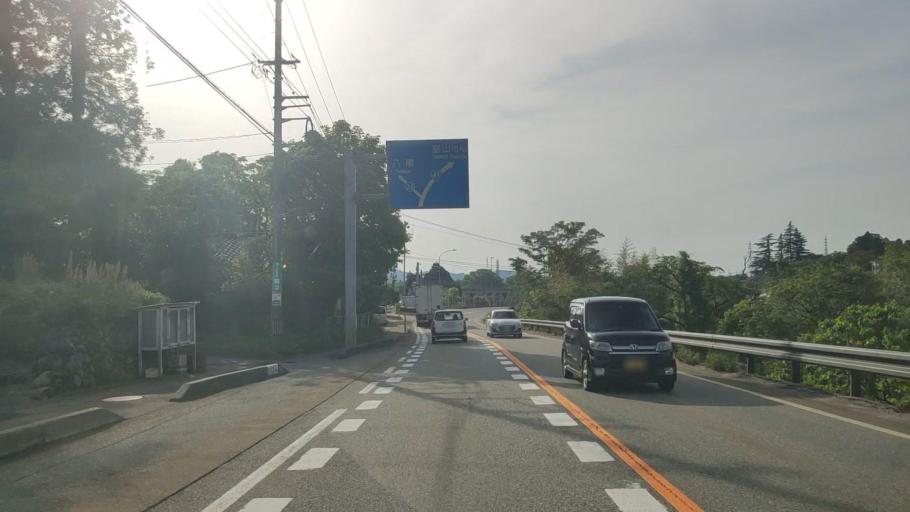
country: JP
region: Toyama
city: Yatsuomachi-higashikumisaka
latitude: 36.5564
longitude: 137.2171
